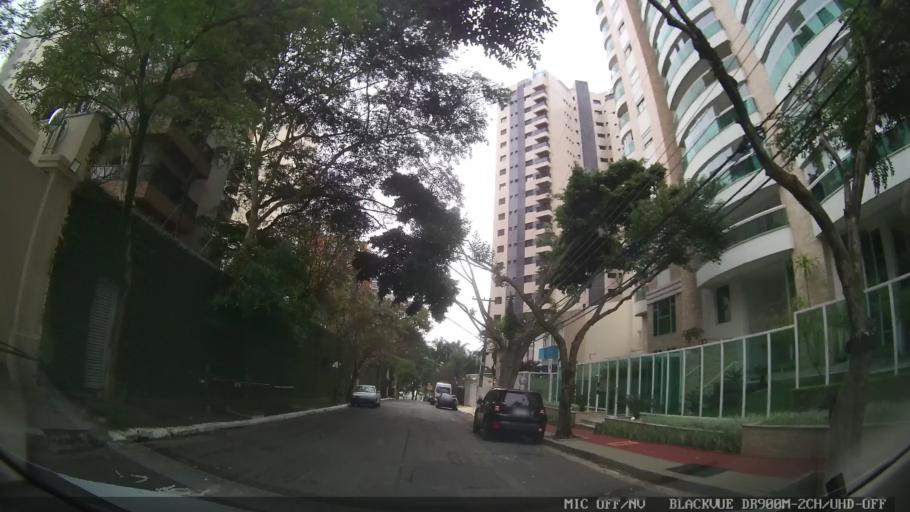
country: BR
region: Sao Paulo
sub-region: Sao Paulo
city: Sao Paulo
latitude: -23.5917
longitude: -46.6243
